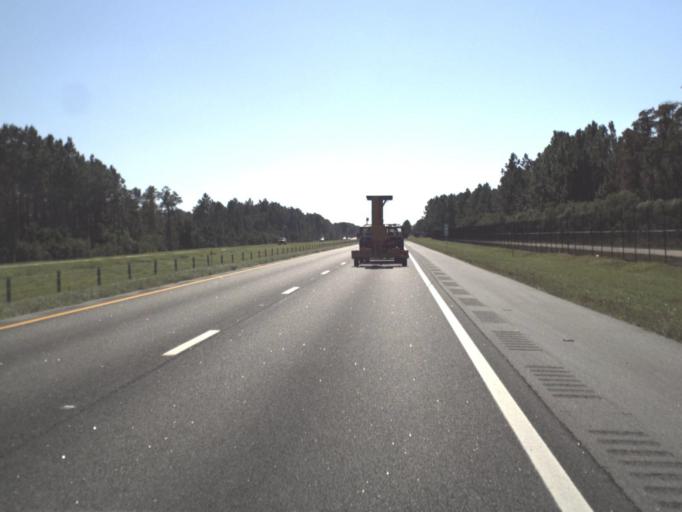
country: US
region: Florida
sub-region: Pasco County
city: Odessa
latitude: 28.2231
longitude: -82.5500
